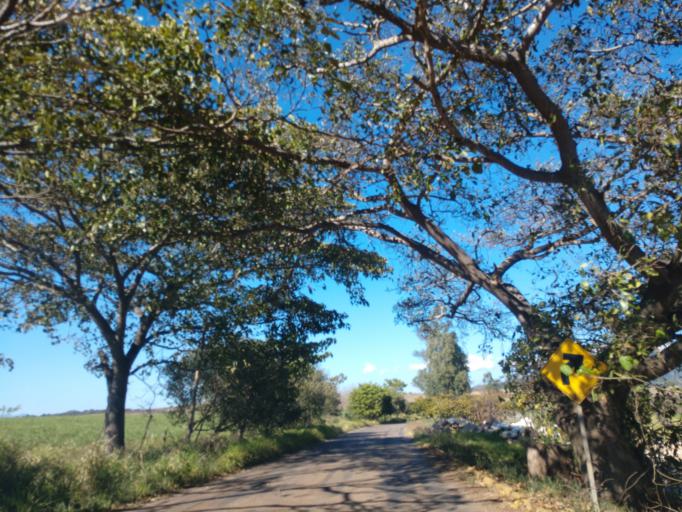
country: MX
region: Nayarit
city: Compostela
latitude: 21.2595
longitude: -104.8972
